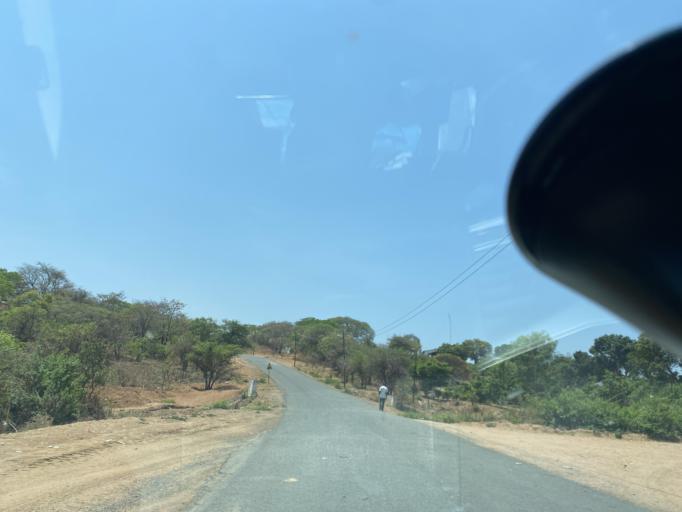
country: ZM
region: Lusaka
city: Kafue
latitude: -15.8679
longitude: 28.4365
